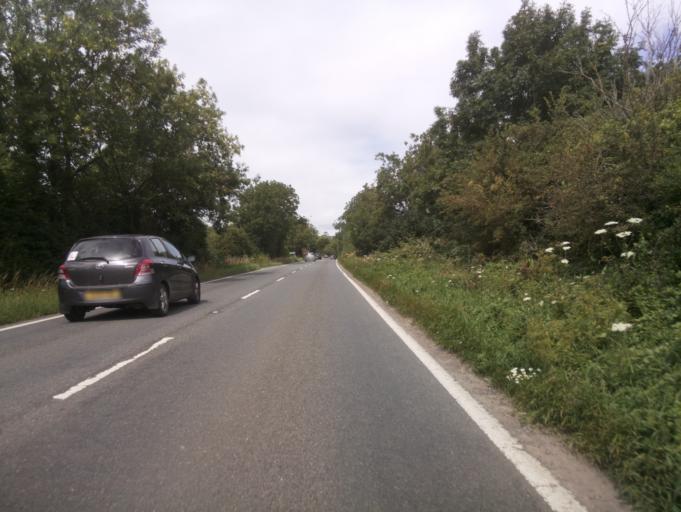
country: GB
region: England
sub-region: Somerset
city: Glastonbury
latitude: 51.1735
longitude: -2.6948
